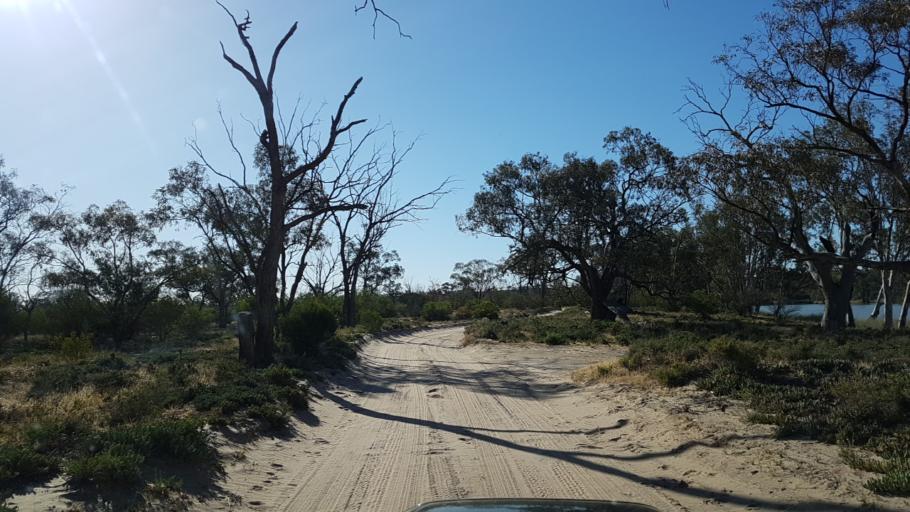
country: AU
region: South Australia
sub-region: Loxton Waikerie
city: Waikerie
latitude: -34.1596
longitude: 140.0291
